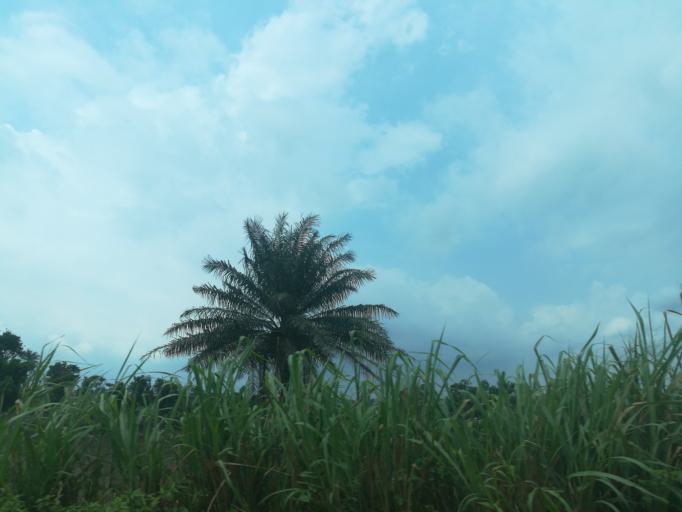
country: NG
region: Lagos
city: Ikorodu
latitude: 6.6718
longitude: 3.6635
